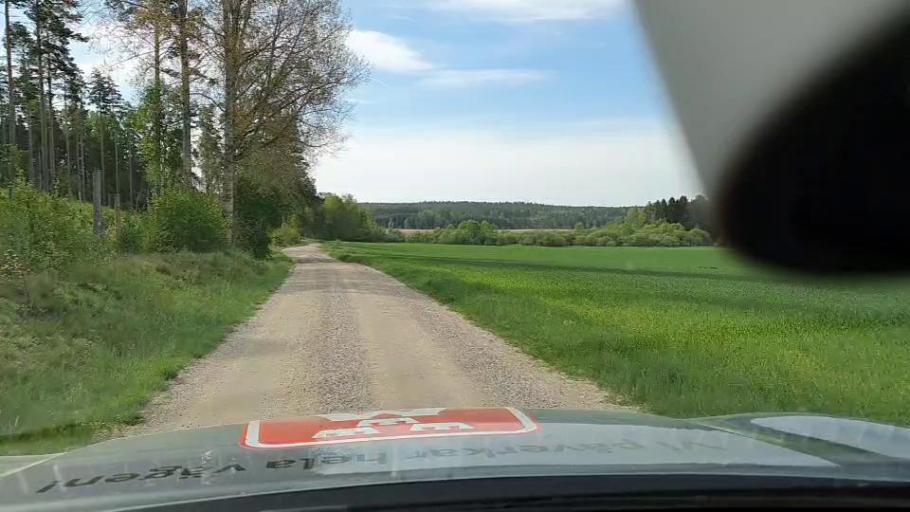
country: SE
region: Soedermanland
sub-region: Strangnas Kommun
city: Akers Styckebruk
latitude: 59.2437
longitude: 16.9338
